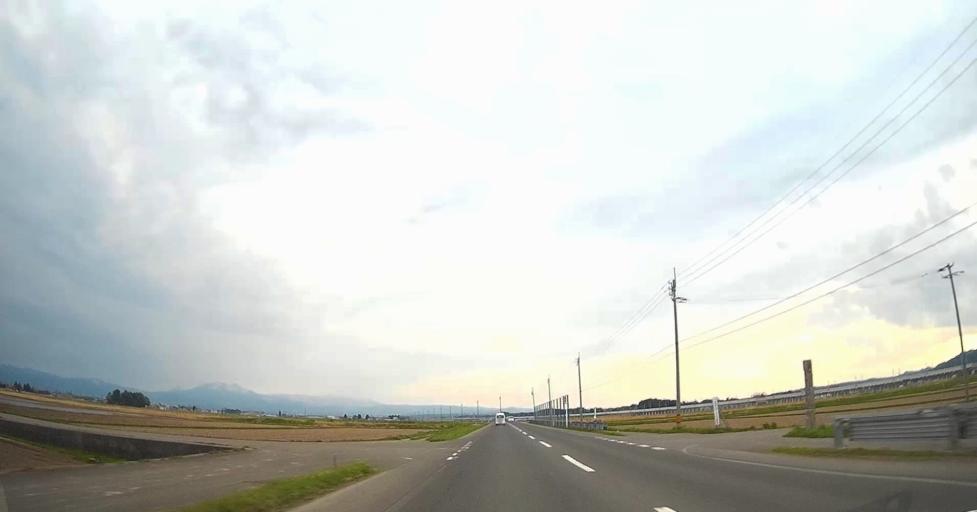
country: JP
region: Aomori
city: Aomori Shi
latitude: 40.8801
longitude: 140.6708
